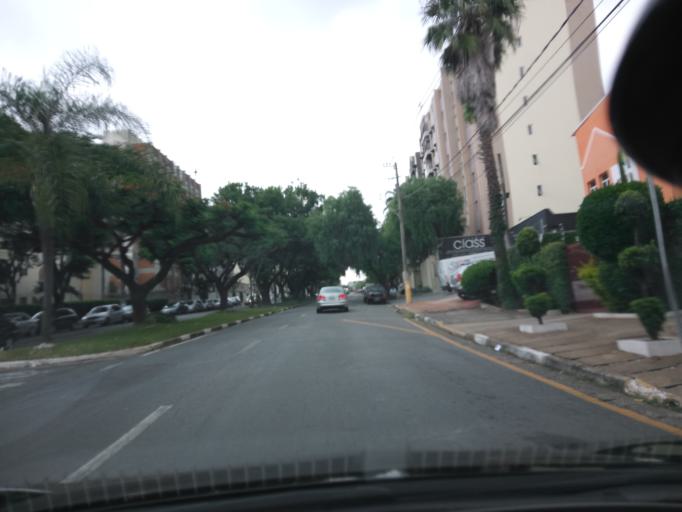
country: BR
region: Sao Paulo
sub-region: Campinas
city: Campinas
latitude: -22.8874
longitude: -47.0313
